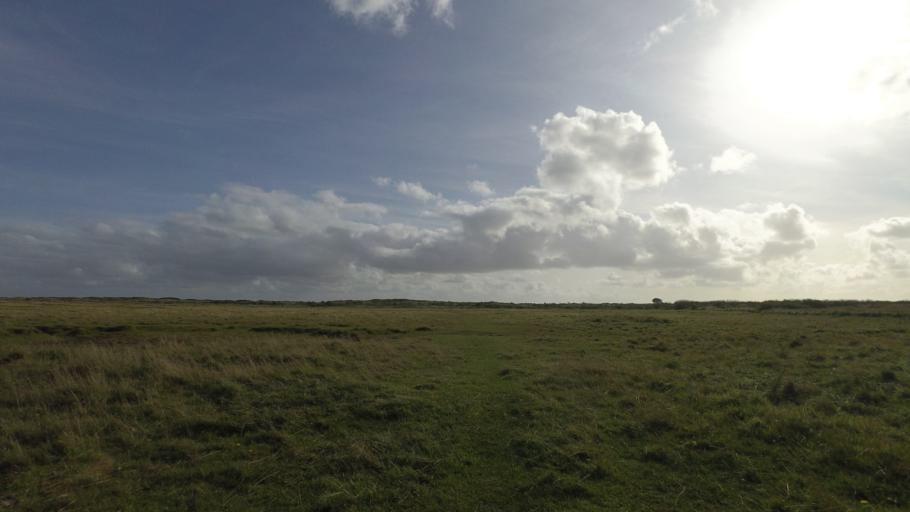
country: NL
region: Friesland
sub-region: Gemeente Ameland
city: Nes
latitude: 53.4602
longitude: 5.8363
